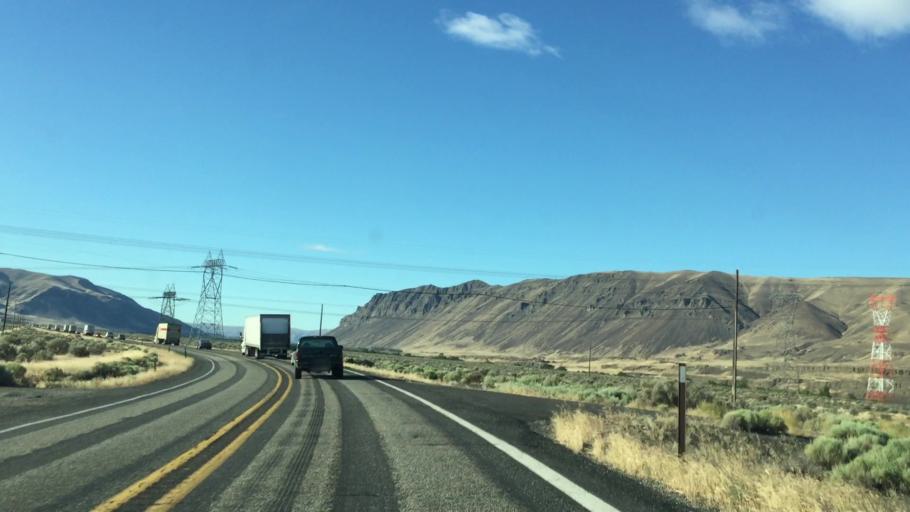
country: US
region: Washington
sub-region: Grant County
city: Mattawa
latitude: 46.8710
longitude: -119.9566
